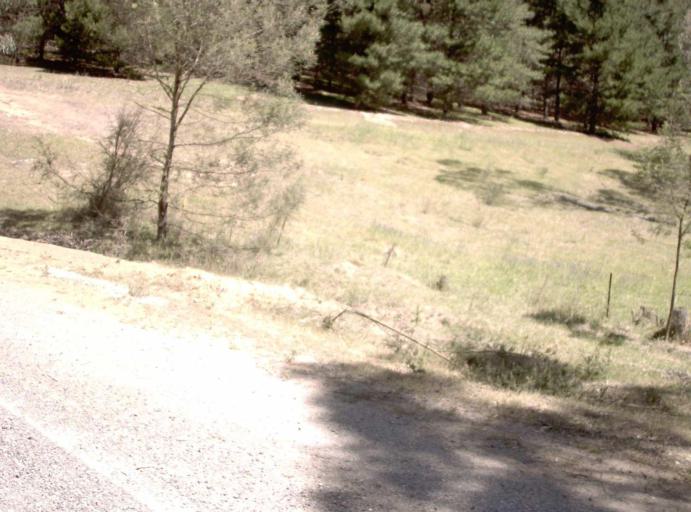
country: AU
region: New South Wales
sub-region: Bombala
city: Bombala
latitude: -37.1120
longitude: 148.6442
